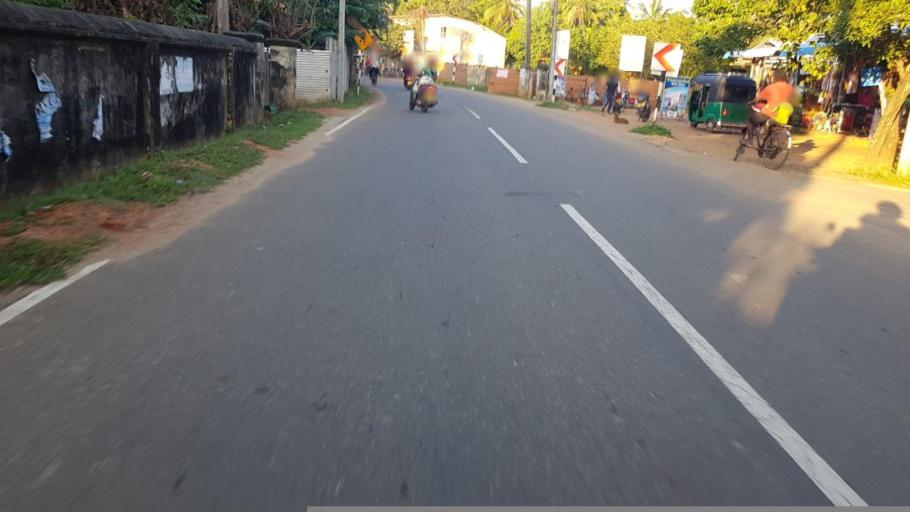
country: LK
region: Northern Province
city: Jaffna
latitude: 9.7344
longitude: 79.9523
